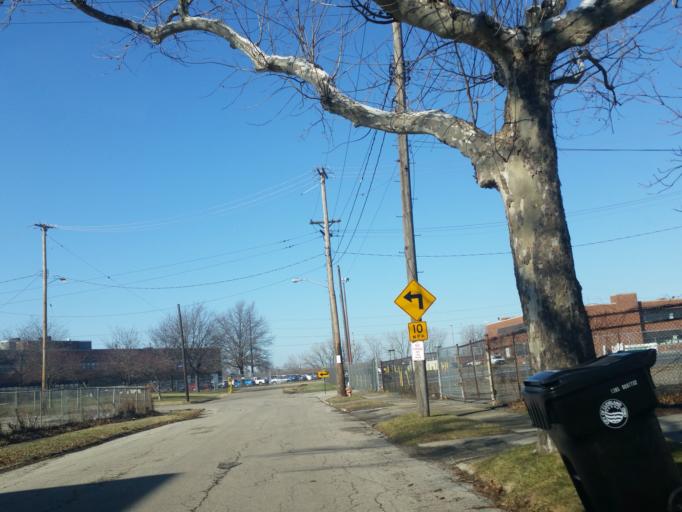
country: US
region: Ohio
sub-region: Cuyahoga County
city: Bratenahl
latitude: 41.5255
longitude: -81.6492
